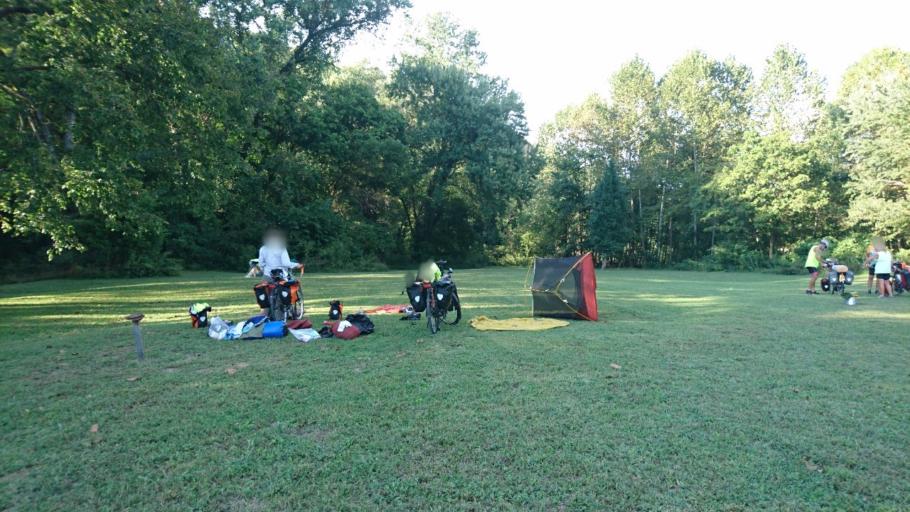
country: US
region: Missouri
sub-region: Pulaski County
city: Waynesville
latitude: 37.8306
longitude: -92.2066
